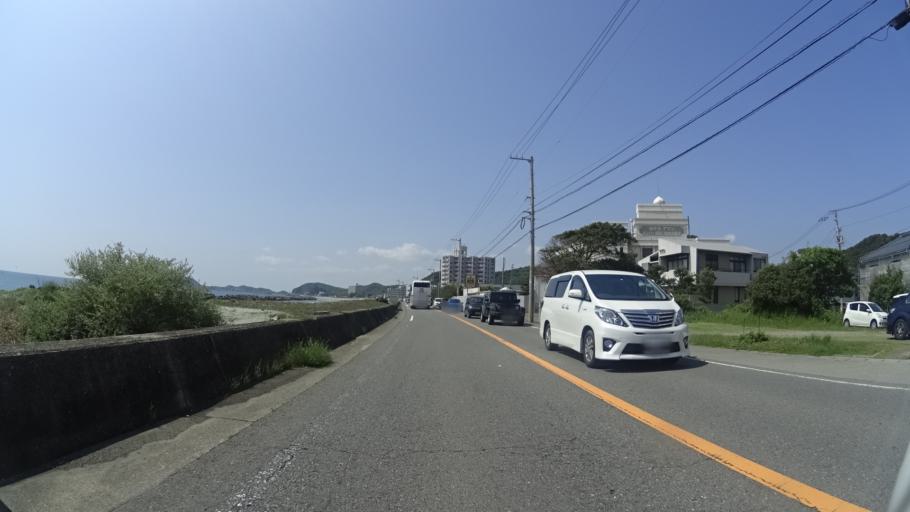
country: JP
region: Tokushima
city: Narutocho-mitsuishi
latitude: 34.2119
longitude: 134.6286
